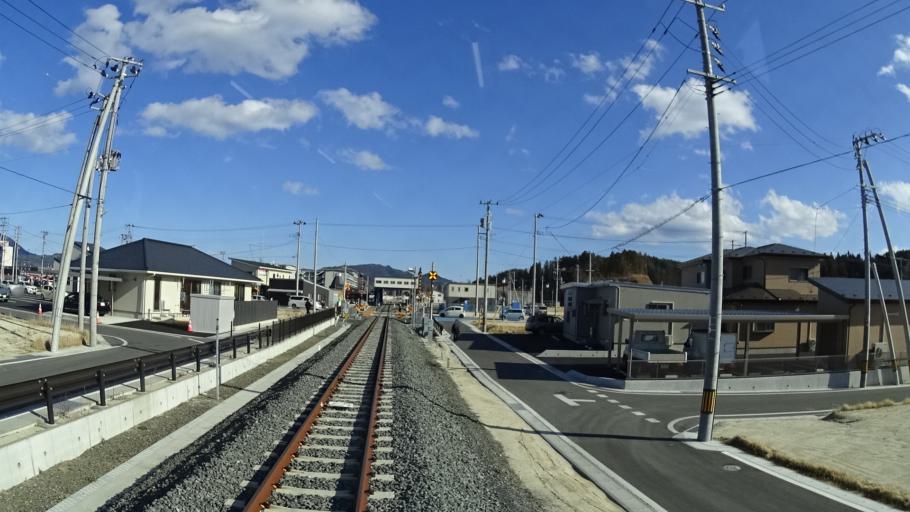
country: JP
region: Iwate
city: Yamada
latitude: 39.4650
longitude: 141.9492
